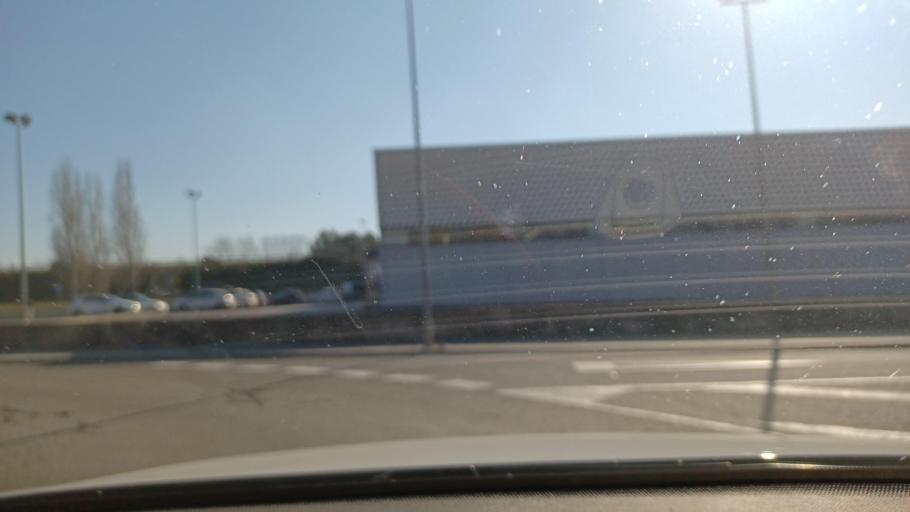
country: ES
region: Catalonia
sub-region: Provincia de Barcelona
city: Vilafranca del Penedes
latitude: 41.3356
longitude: 1.6825
